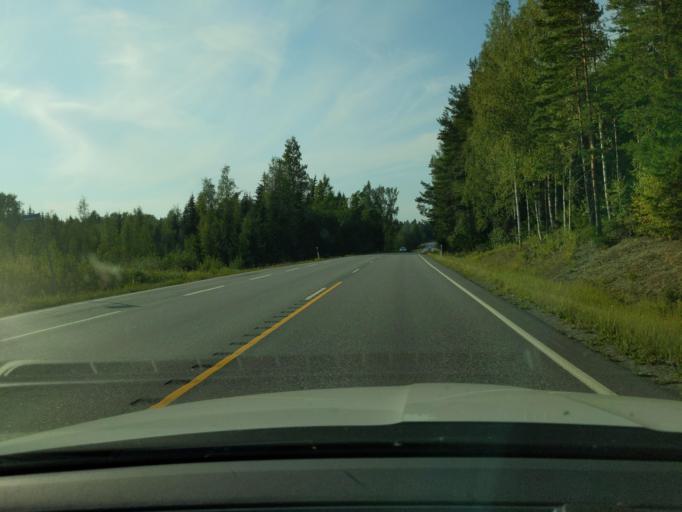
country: FI
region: Paijanne Tavastia
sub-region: Lahti
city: Padasjoki
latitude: 61.3207
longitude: 25.2817
